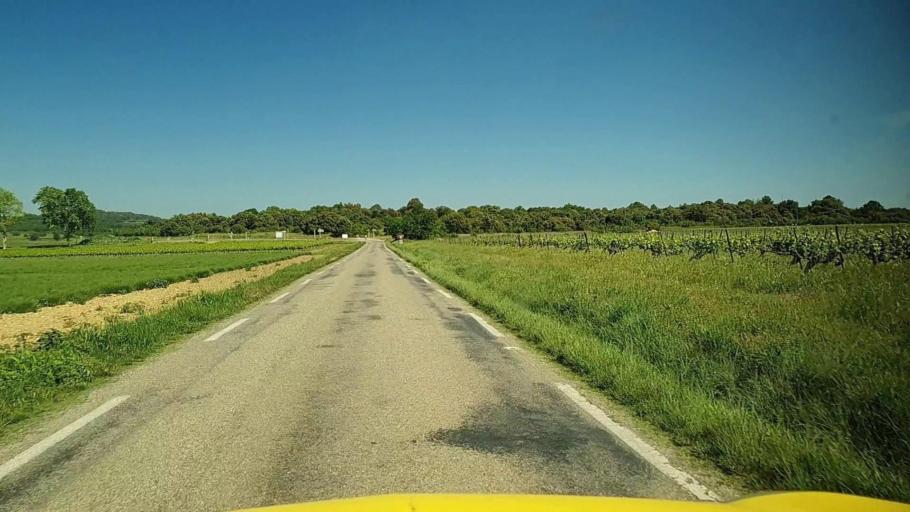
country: FR
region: Languedoc-Roussillon
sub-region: Departement du Gard
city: Saint-Chaptes
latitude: 43.9837
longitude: 4.2737
